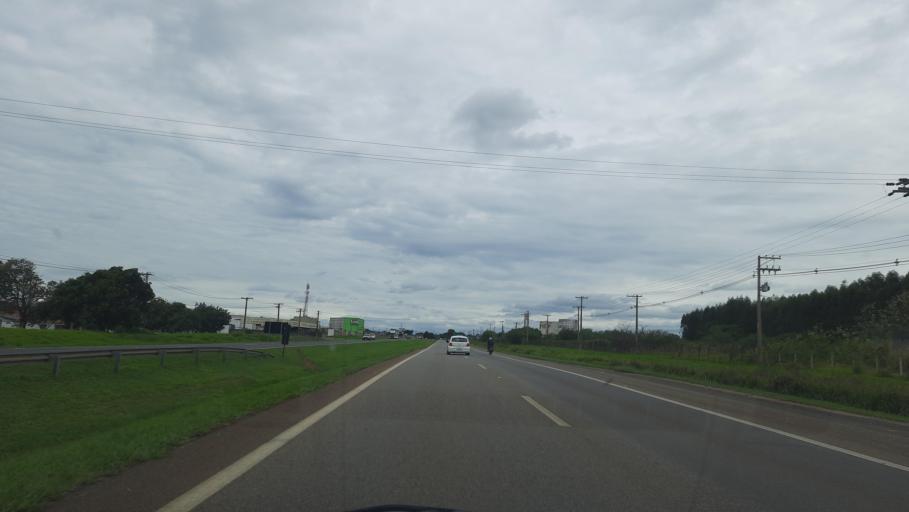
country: BR
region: Sao Paulo
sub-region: Moji-Guacu
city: Mogi-Gaucu
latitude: -22.3391
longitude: -46.9582
